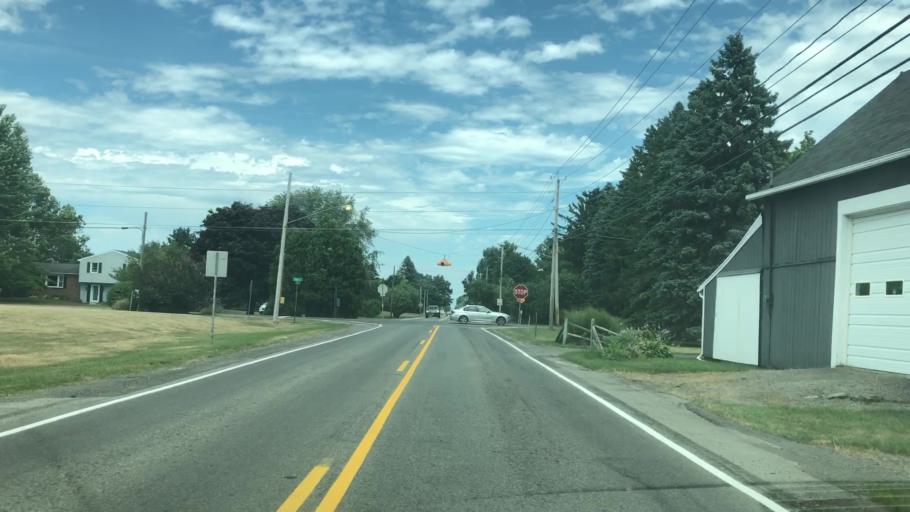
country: US
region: New York
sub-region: Monroe County
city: Webster
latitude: 43.1811
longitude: -77.4004
